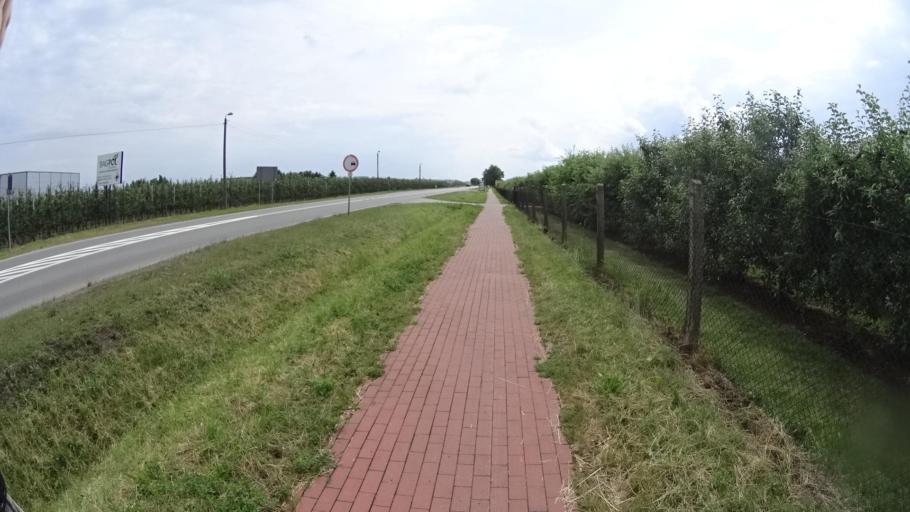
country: PL
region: Masovian Voivodeship
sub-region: Powiat grojecki
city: Grojec
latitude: 51.8879
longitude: 20.8627
